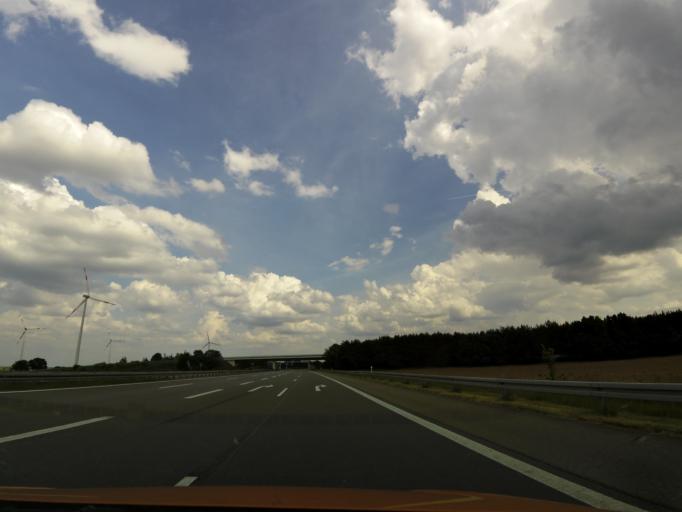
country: DE
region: Brandenburg
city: Wittstock
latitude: 53.1360
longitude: 12.4444
